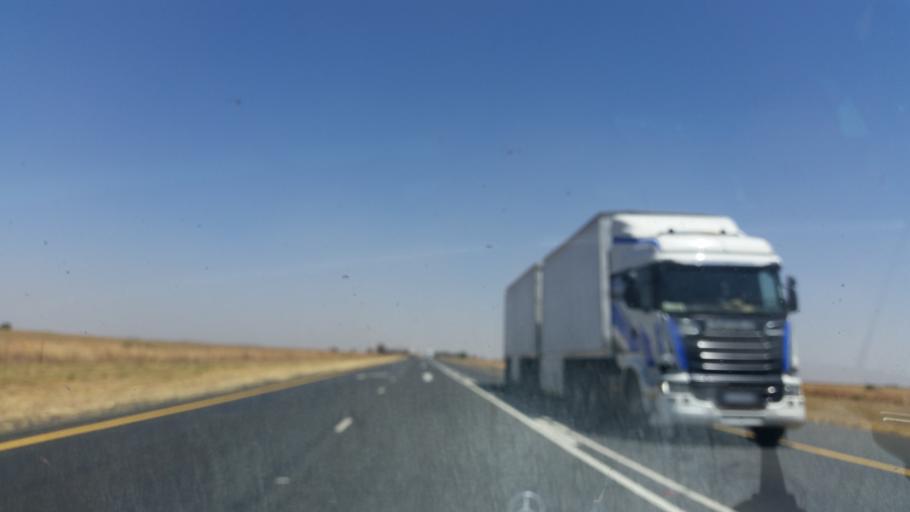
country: ZA
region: Orange Free State
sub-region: Lejweleputswa District Municipality
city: Winburg
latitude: -28.6459
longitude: 26.8825
